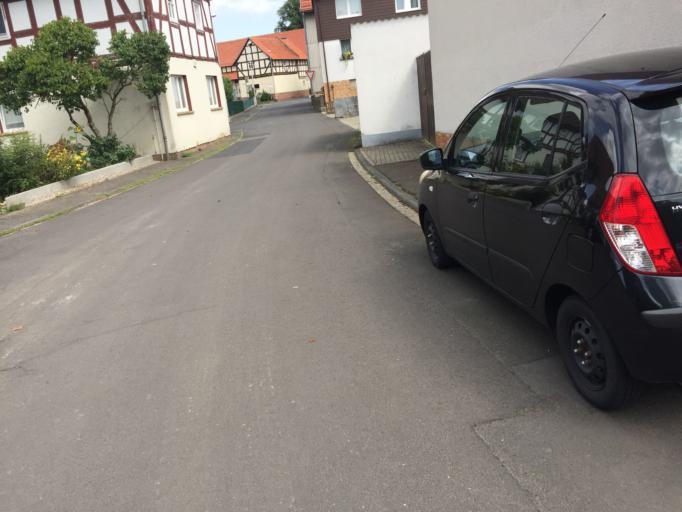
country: DE
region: Hesse
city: Schwalmstadt
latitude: 50.9147
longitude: 9.2575
